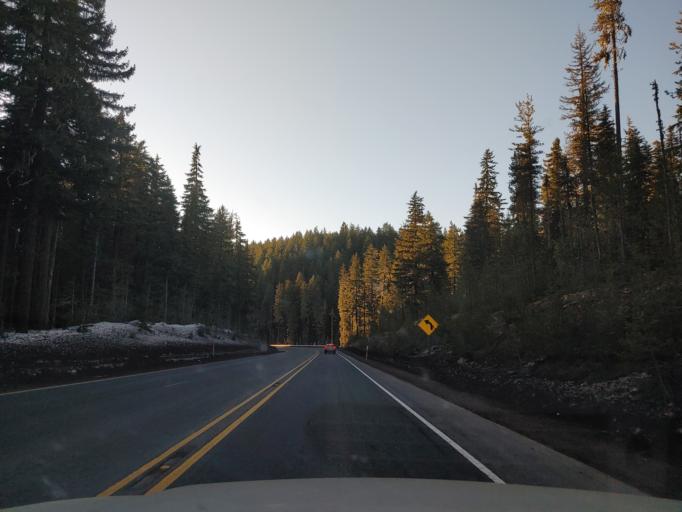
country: US
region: Oregon
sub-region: Lane County
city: Oakridge
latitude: 43.6101
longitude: -122.0586
